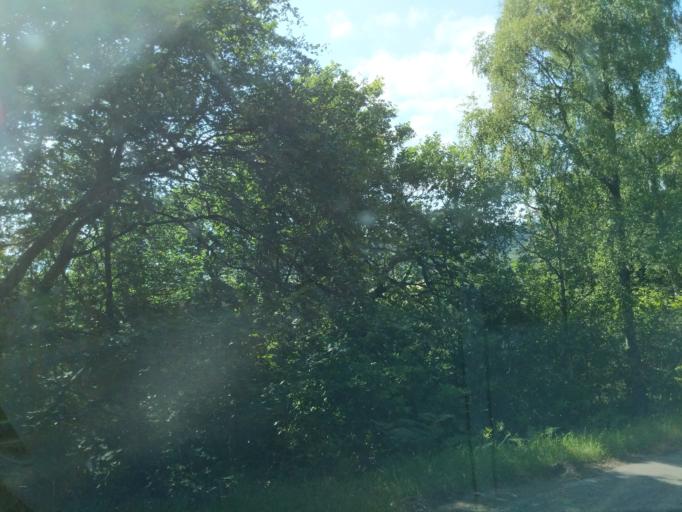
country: GB
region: Scotland
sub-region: Moray
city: Fochabers
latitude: 57.5521
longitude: -3.1369
